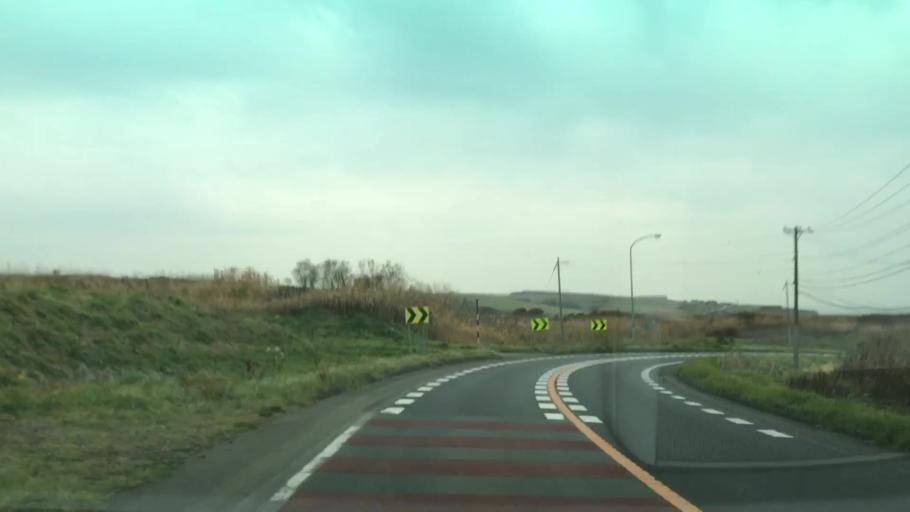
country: JP
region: Hokkaido
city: Ishikari
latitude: 43.3616
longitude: 141.4310
